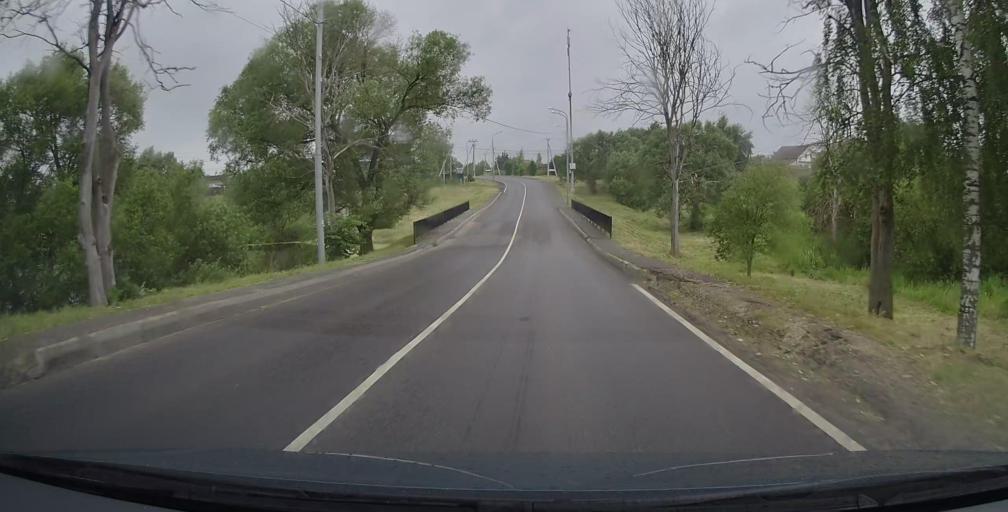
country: RU
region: Moskovskaya
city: Selyatino
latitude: 55.4293
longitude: 36.9615
